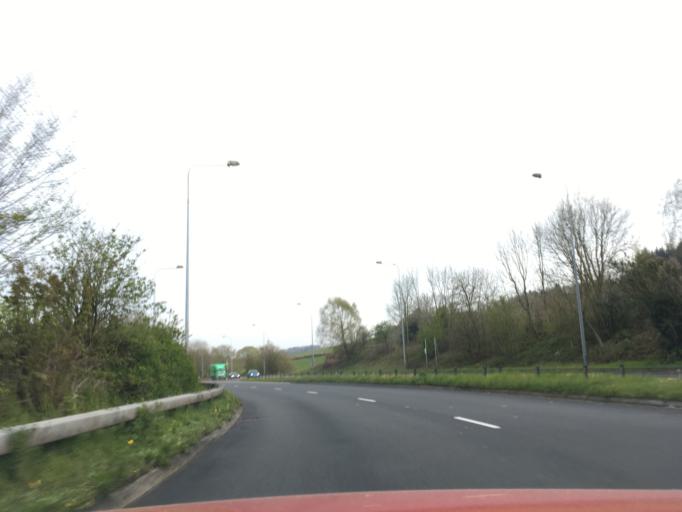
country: GB
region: Wales
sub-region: Caerphilly County Borough
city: Risca
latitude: 51.5949
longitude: -3.0777
